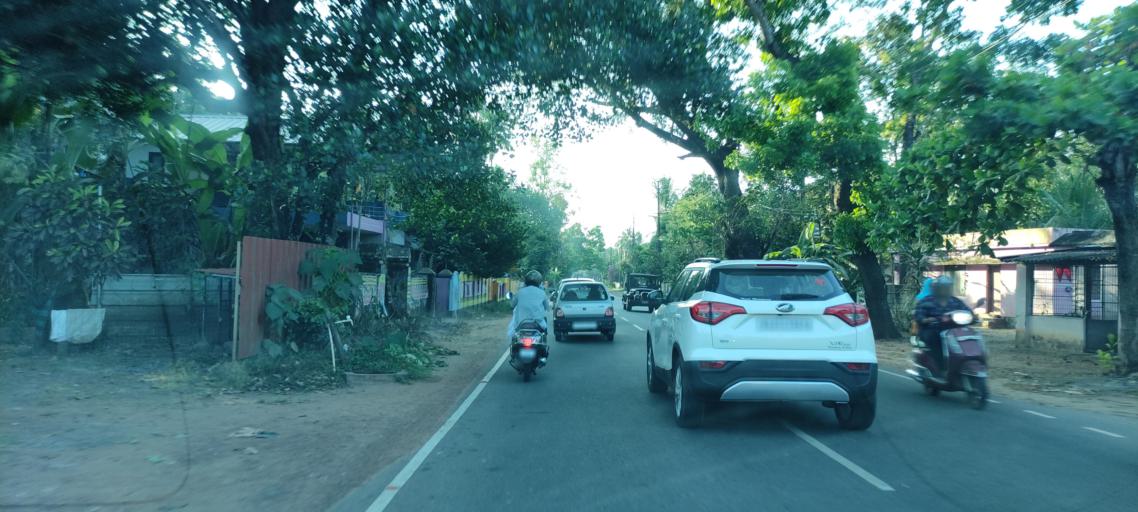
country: IN
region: Kerala
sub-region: Alappuzha
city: Kattanam
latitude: 9.1743
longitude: 76.5789
